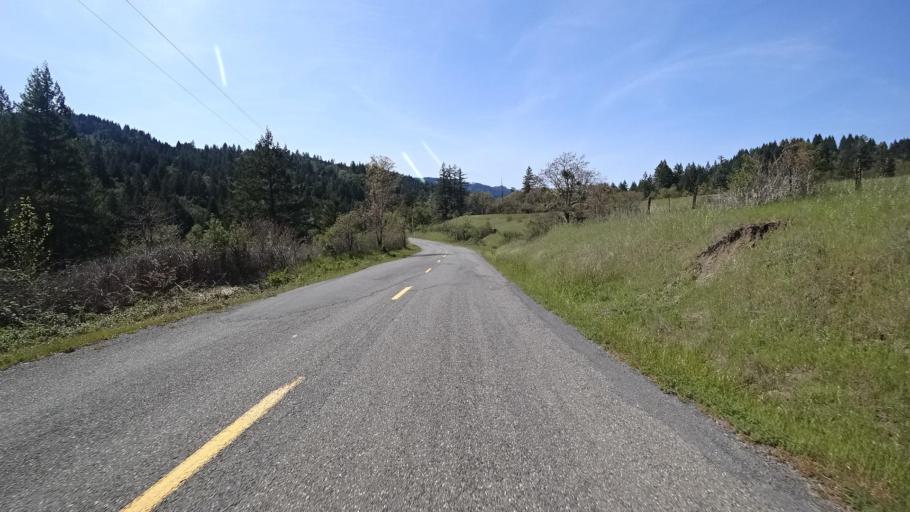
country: US
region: California
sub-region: Humboldt County
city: Redway
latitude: 40.3406
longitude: -123.7035
